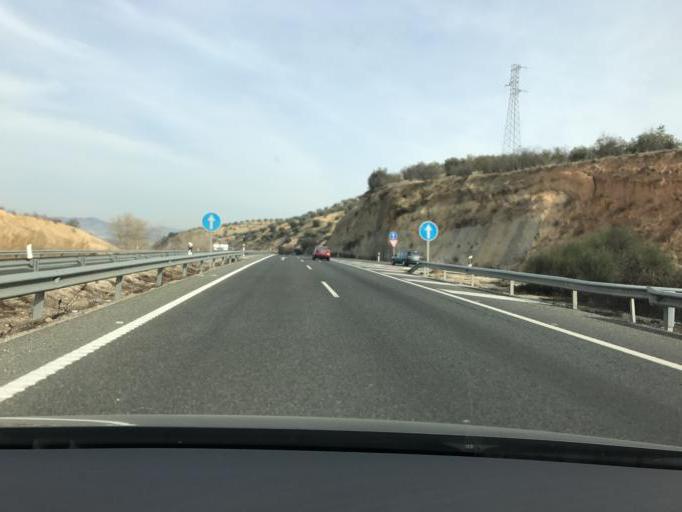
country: ES
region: Andalusia
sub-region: Provincia de Granada
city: Salar
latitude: 37.1701
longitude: -4.0847
